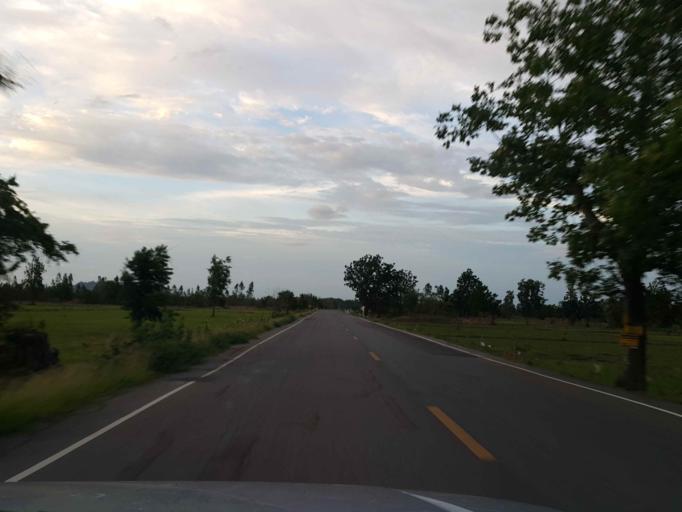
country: TH
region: Sukhothai
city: Ban Dan Lan Hoi
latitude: 17.0905
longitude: 99.5894
